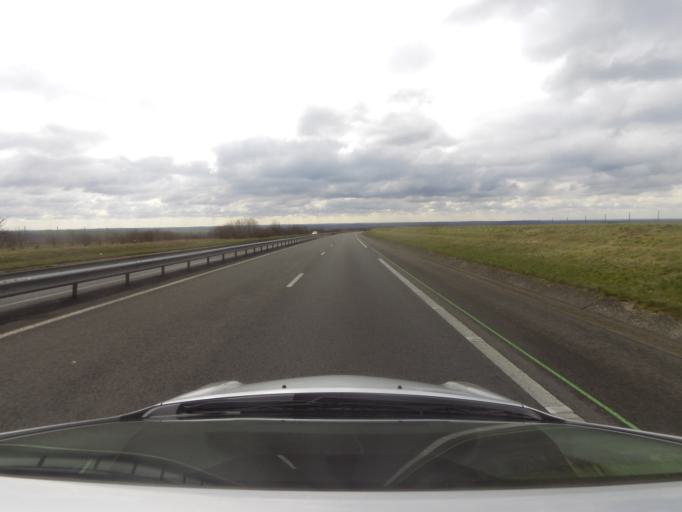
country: FR
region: Nord-Pas-de-Calais
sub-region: Departement du Pas-de-Calais
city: Etaples
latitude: 50.5490
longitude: 1.6744
